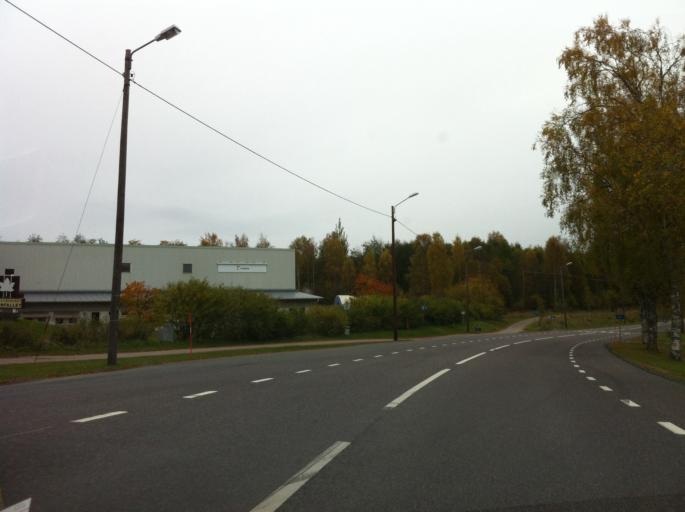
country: SE
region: Dalarna
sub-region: Ludvika Kommun
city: Grangesberg
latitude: 60.0668
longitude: 14.9865
